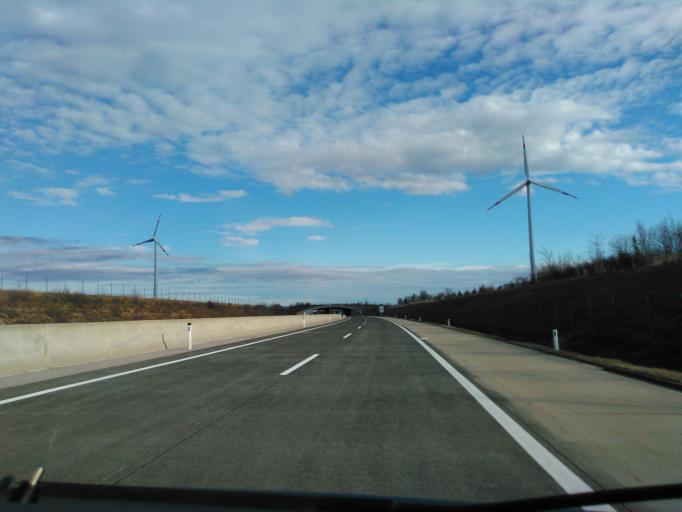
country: AT
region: Burgenland
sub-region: Politischer Bezirk Neusiedl am See
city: Potzneusiedl
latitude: 48.0306
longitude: 16.9202
